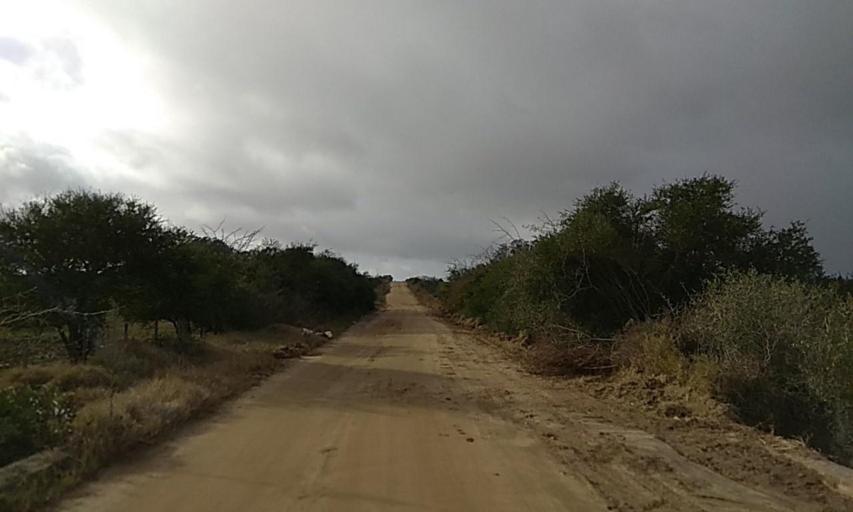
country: UY
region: Florida
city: Florida
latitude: -34.0597
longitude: -56.2125
